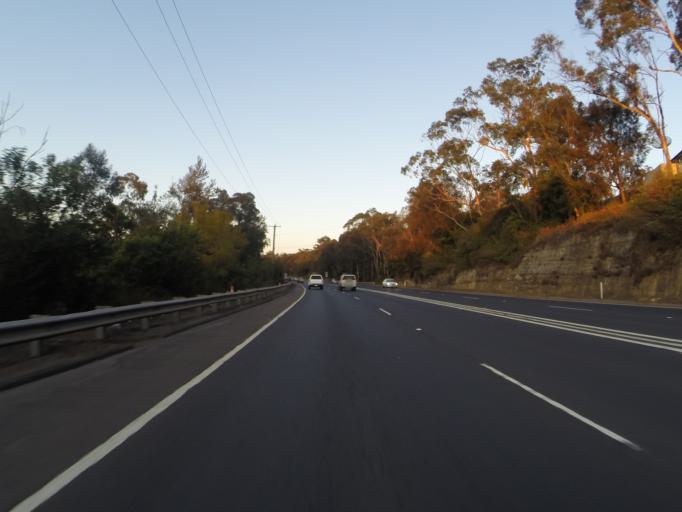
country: AU
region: New South Wales
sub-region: Blue Mountains Municipality
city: Glenbrook
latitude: -33.7644
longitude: 150.6281
